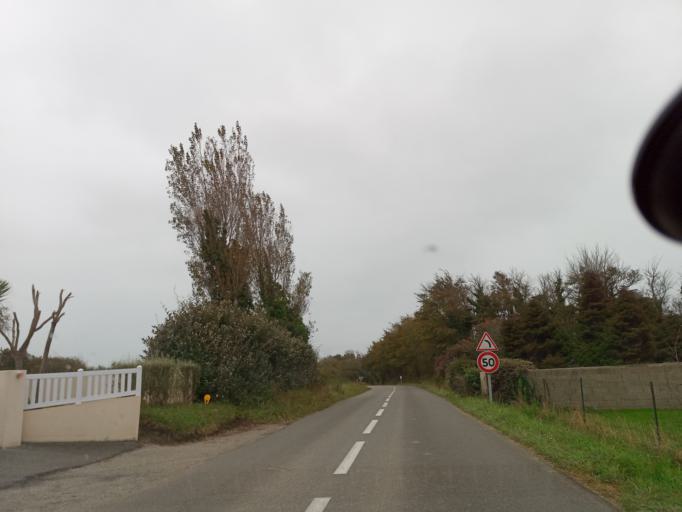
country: FR
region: Brittany
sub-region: Departement du Finistere
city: Esquibien
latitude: 48.0194
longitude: -4.5637
